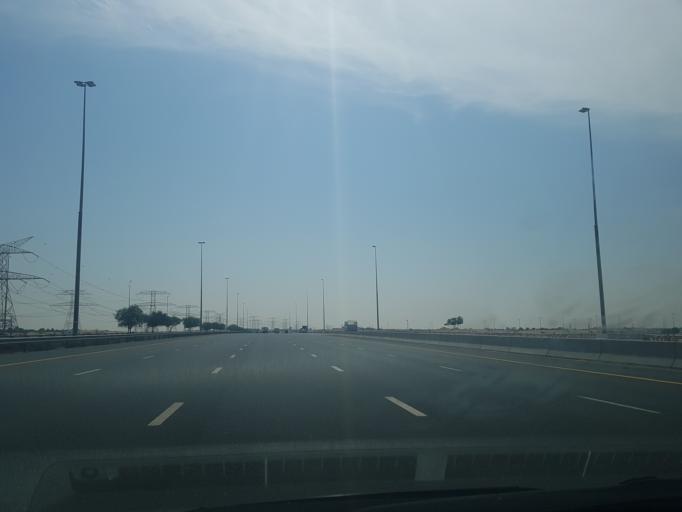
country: AE
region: Ash Shariqah
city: Sharjah
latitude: 25.2250
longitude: 55.5597
